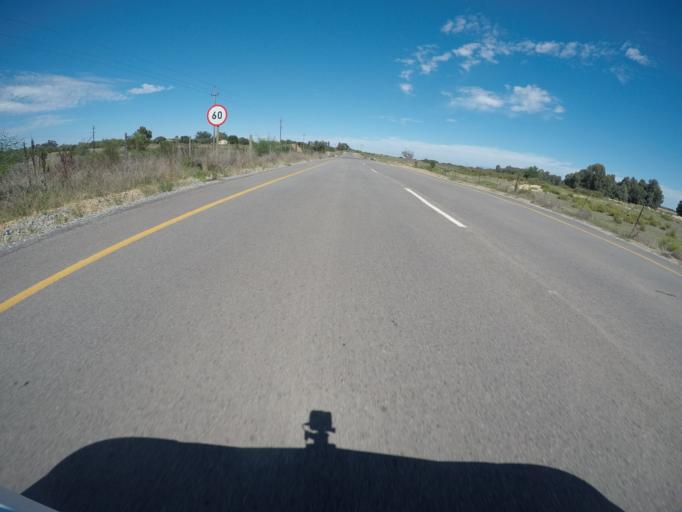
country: ZA
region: Western Cape
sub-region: West Coast District Municipality
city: Malmesbury
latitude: -33.5826
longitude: 18.6468
